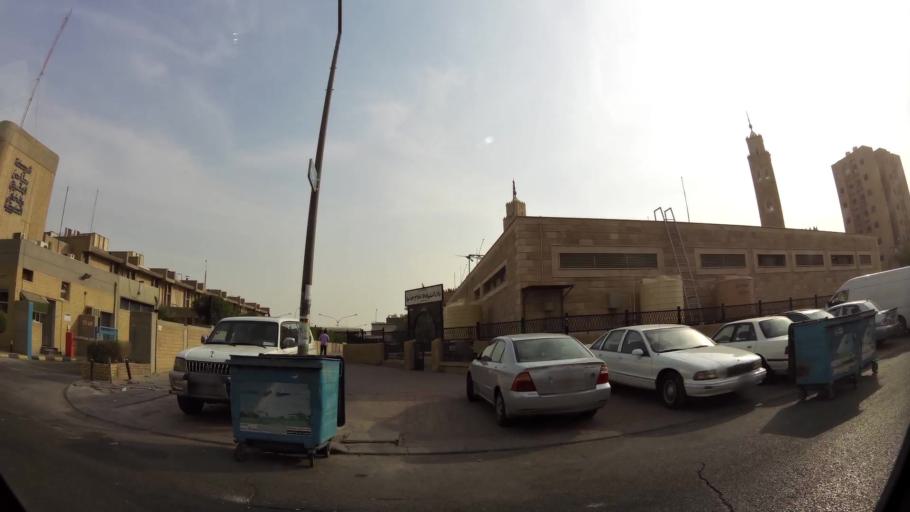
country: KW
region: Al Farwaniyah
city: Al Farwaniyah
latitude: 29.2950
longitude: 47.9702
